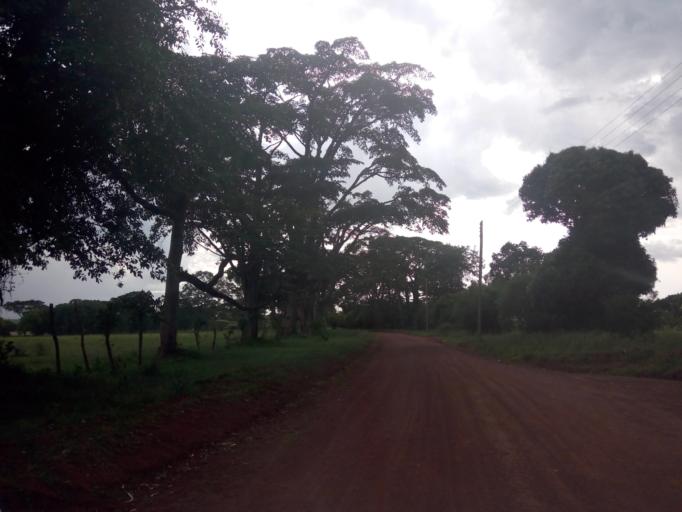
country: UG
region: Western Region
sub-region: Masindi District
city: Masindi
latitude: 1.6917
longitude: 31.7210
